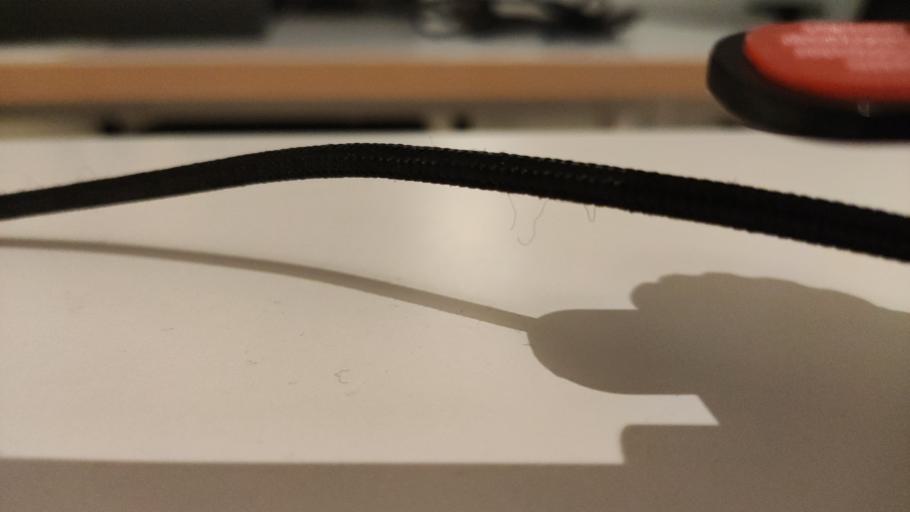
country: RU
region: Moskovskaya
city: Novoye
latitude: 55.6333
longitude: 38.9345
